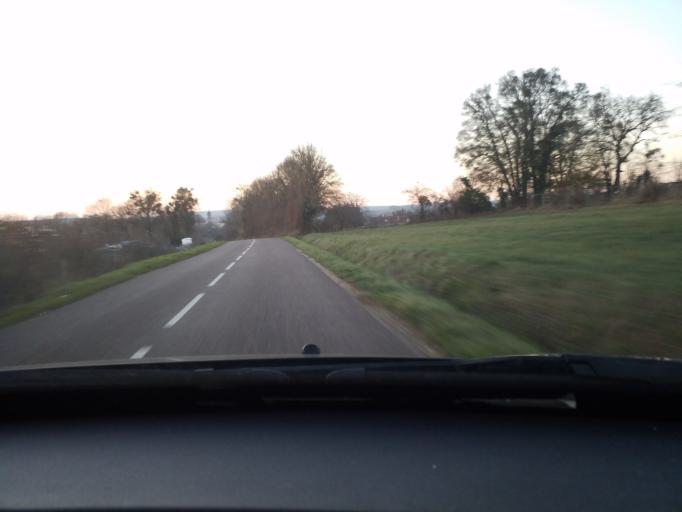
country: FR
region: Franche-Comte
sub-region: Departement de la Haute-Saone
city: Faverney
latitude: 47.8848
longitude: 6.1368
